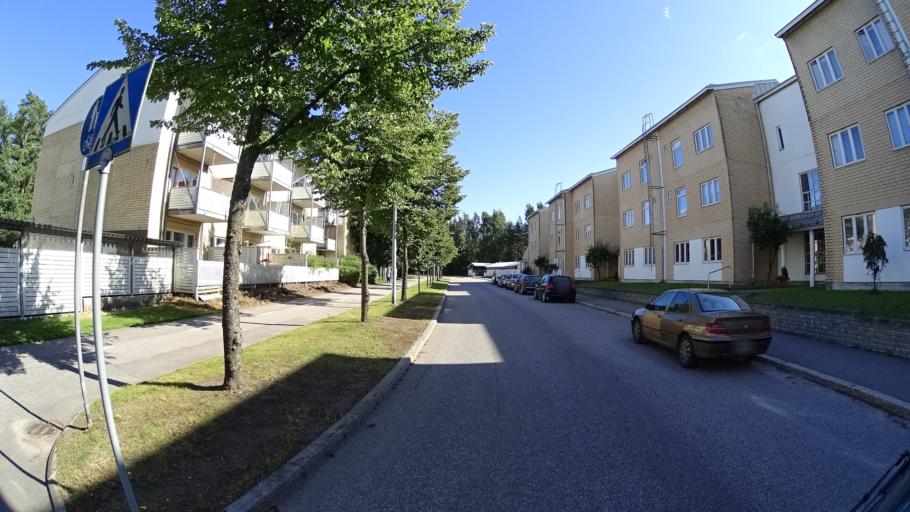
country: FI
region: Uusimaa
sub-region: Helsinki
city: Vantaa
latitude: 60.2300
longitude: 25.0659
